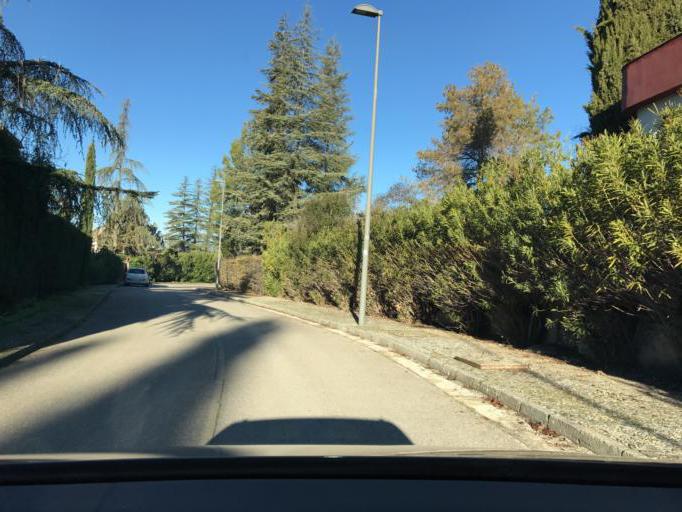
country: ES
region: Andalusia
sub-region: Provincia de Granada
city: Albolote
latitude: 37.2526
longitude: -3.6523
